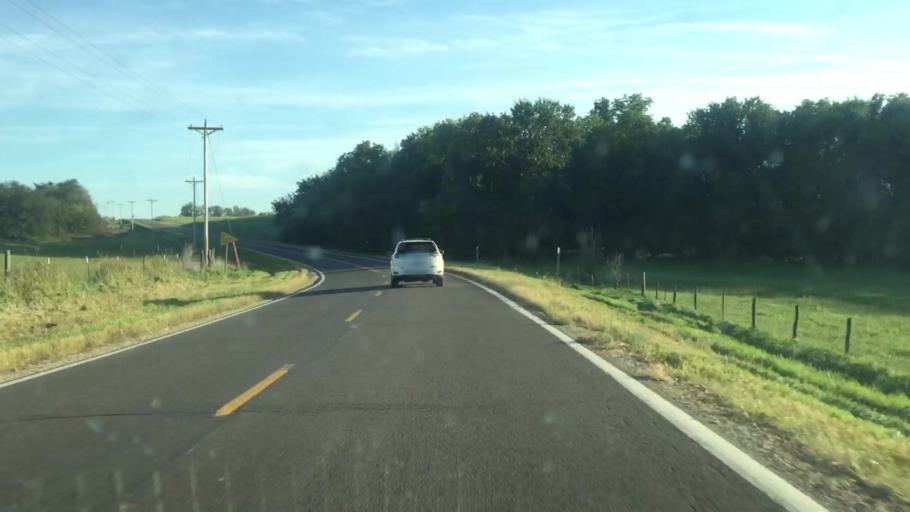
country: US
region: Kansas
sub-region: Brown County
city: Horton
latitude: 39.5703
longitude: -95.5270
